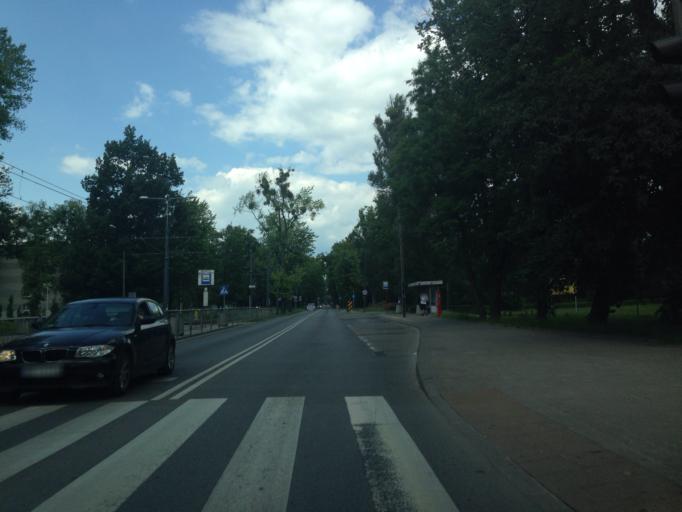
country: PL
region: Masovian Voivodeship
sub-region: Warszawa
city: Bemowo
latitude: 52.2522
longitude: 20.8984
